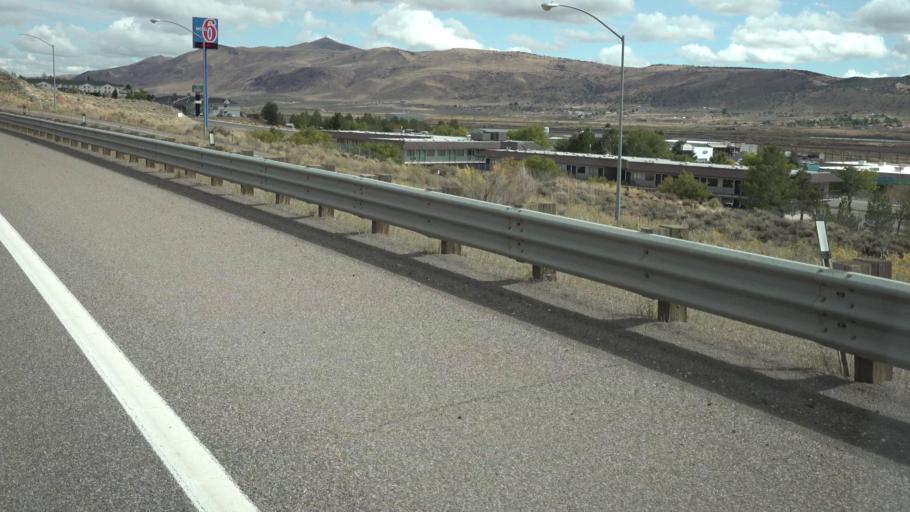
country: US
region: Nevada
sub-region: Elko County
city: Elko
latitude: 40.8534
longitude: -115.7458
